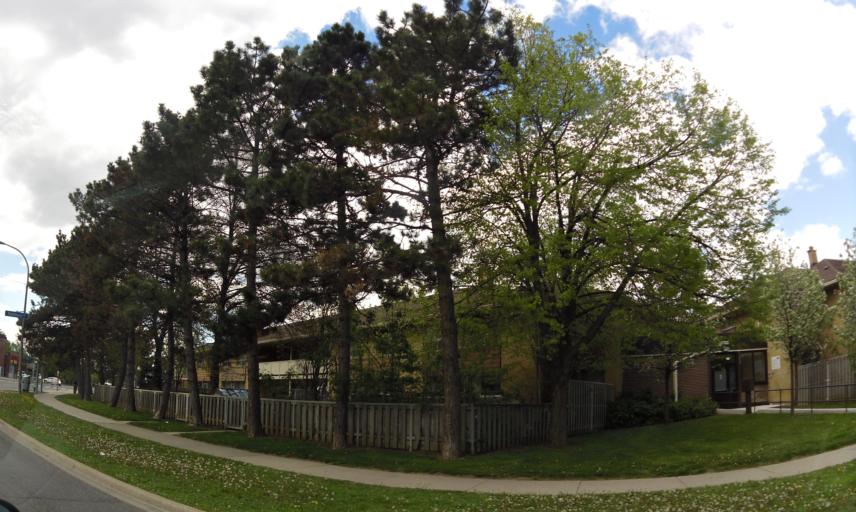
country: CA
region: Ontario
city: Etobicoke
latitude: 43.6524
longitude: -79.5721
